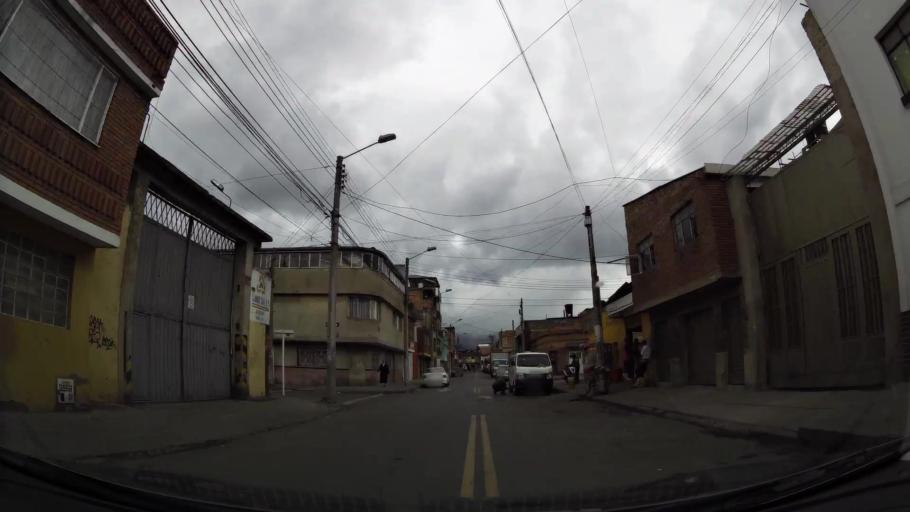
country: CO
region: Bogota D.C.
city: Barrio San Luis
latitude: 4.6987
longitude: -74.1000
